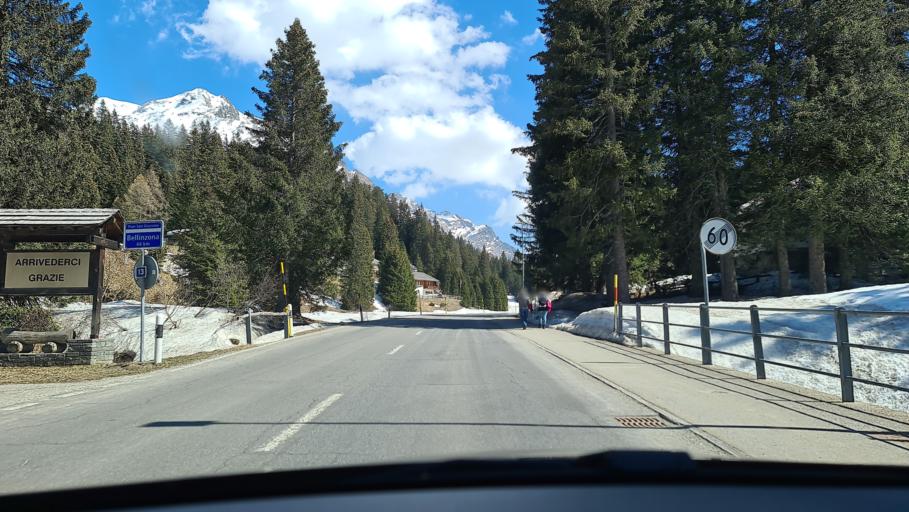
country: CH
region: Grisons
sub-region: Hinterrhein District
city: Hinterrhein
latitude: 46.4579
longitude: 9.1949
